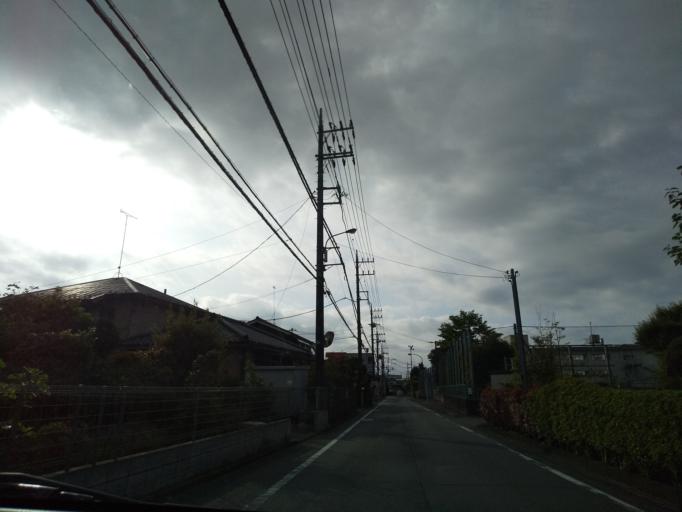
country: JP
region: Tokyo
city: Hachioji
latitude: 35.6890
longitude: 139.3071
